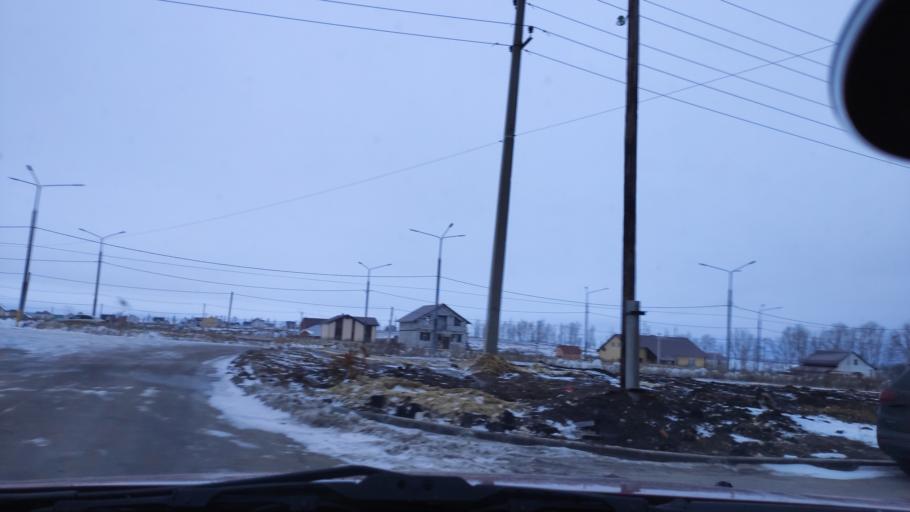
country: RU
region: Tambov
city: Tambov
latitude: 52.7838
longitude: 41.4187
